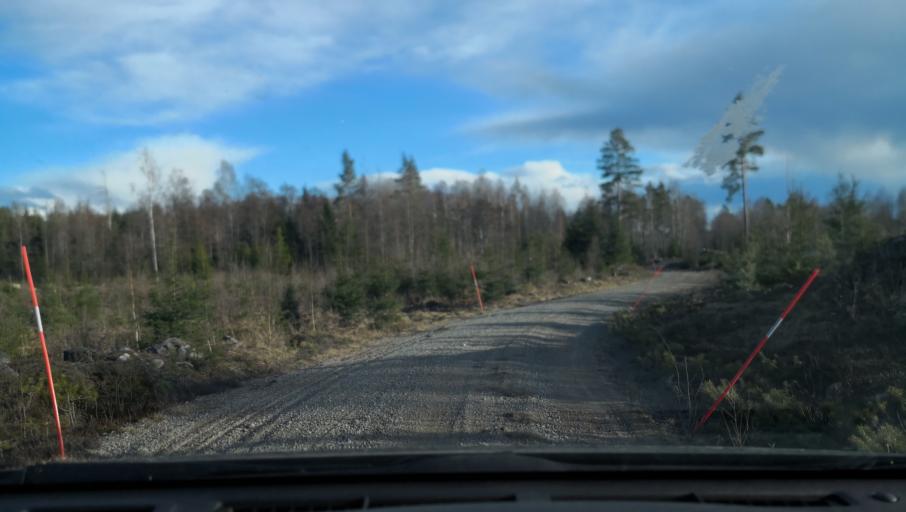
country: SE
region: Vaestmanland
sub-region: Arboga Kommun
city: Arboga
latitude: 59.4323
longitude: 15.7530
